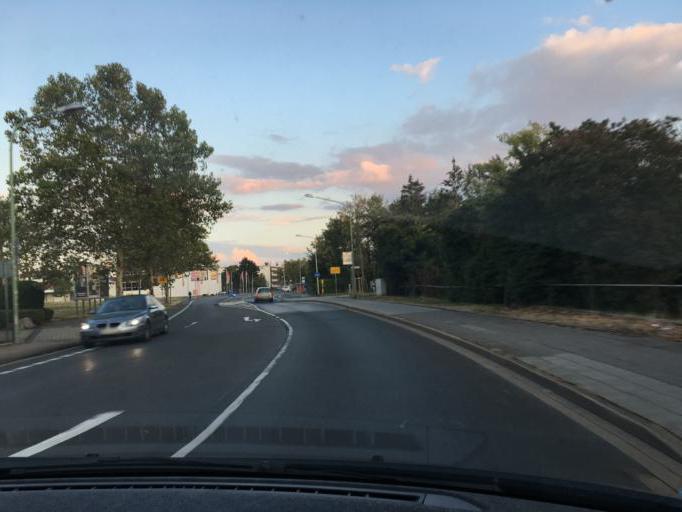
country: DE
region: North Rhine-Westphalia
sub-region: Regierungsbezirk Koln
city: Dueren
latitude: 50.8176
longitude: 6.4673
